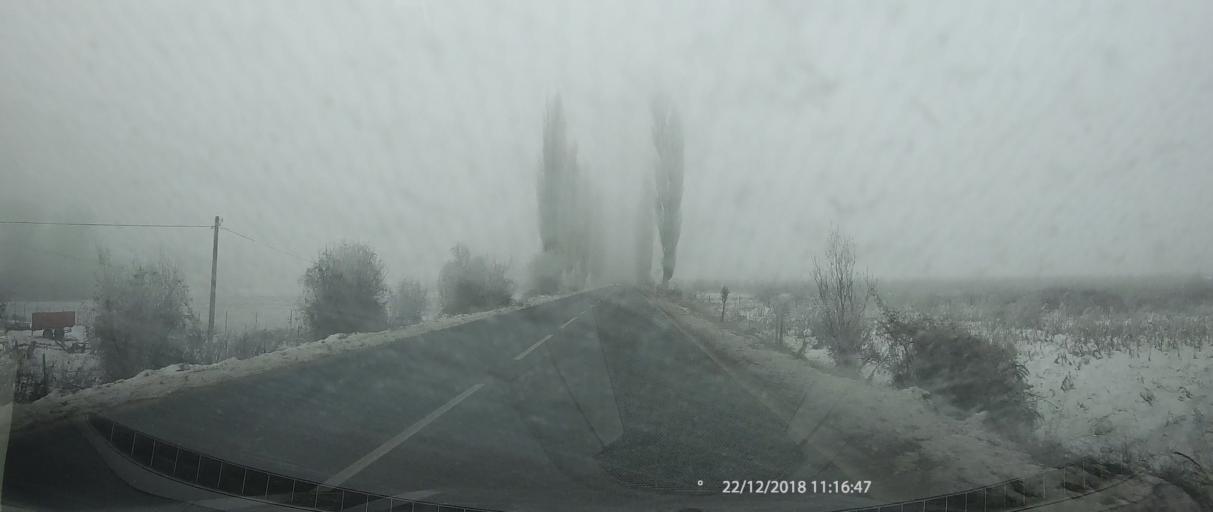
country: BG
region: Kyustendil
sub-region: Obshtina Kyustendil
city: Kyustendil
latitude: 42.2769
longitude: 22.7459
